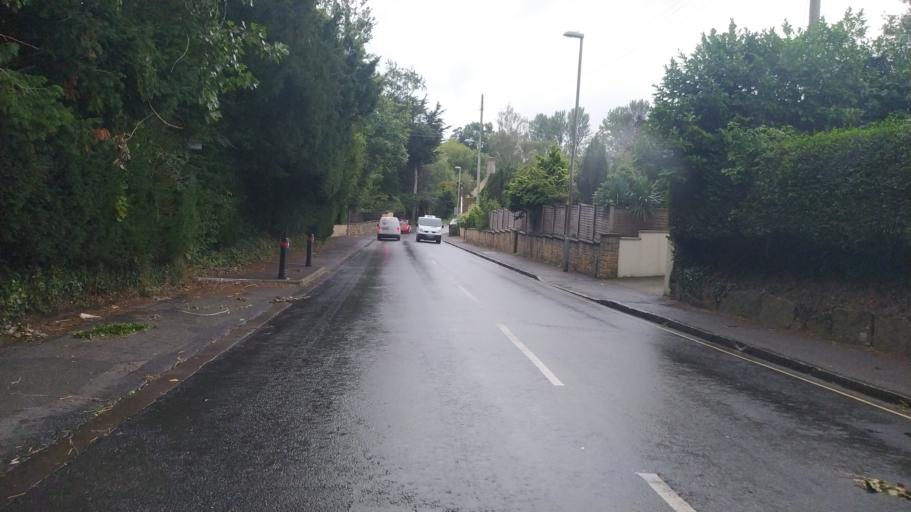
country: GB
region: England
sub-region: Dorset
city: Sturminster Newton
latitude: 50.9239
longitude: -2.3064
